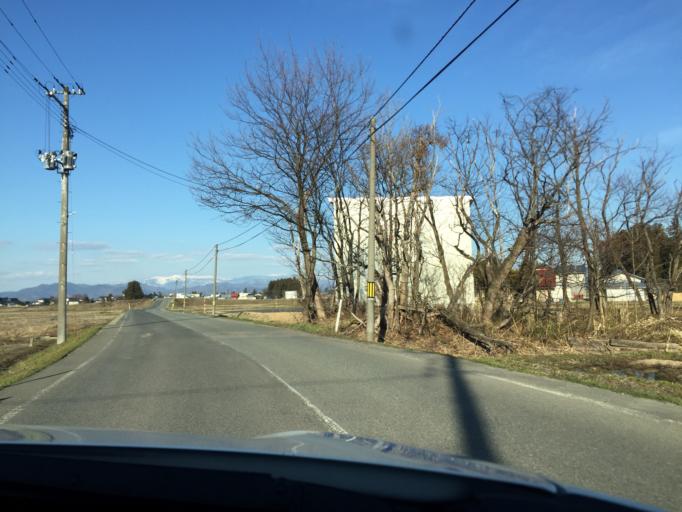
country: JP
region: Yamagata
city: Yonezawa
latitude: 37.9812
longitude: 140.0707
